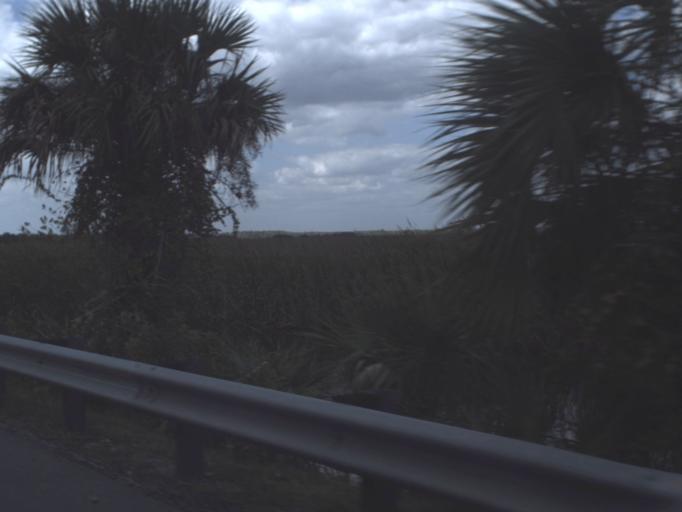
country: US
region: Florida
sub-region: Collier County
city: Marco
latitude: 25.9318
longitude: -81.4428
